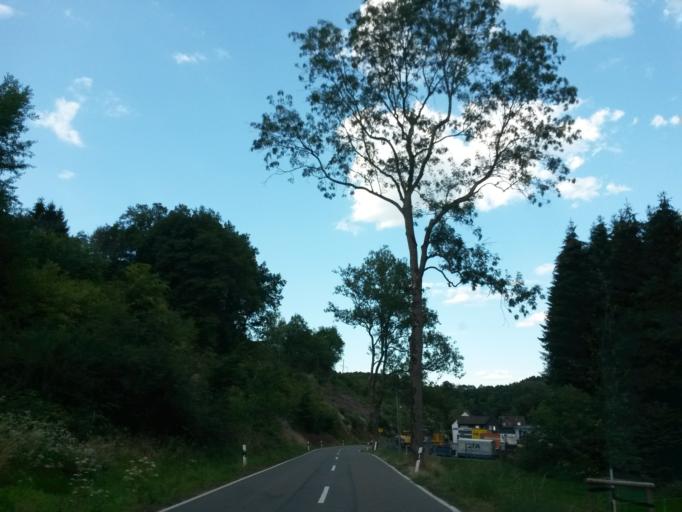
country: DE
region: North Rhine-Westphalia
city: Wiehl
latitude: 50.9568
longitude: 7.4962
